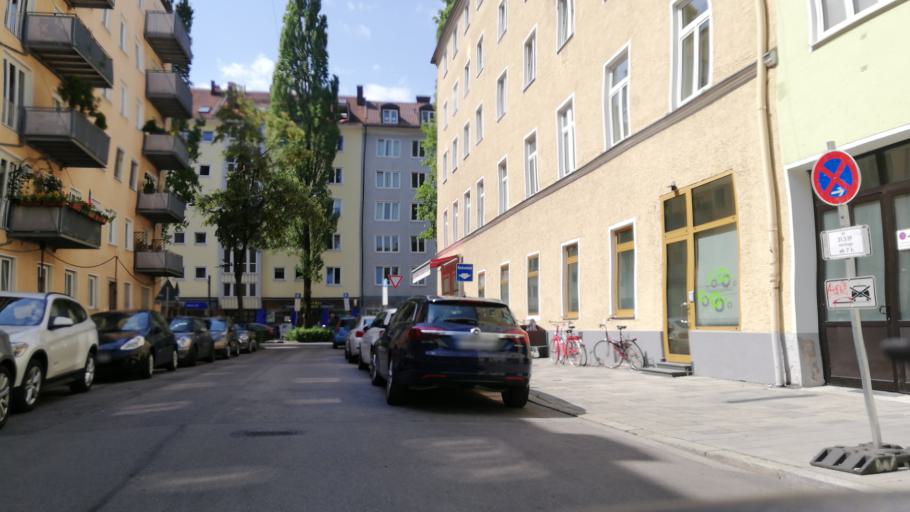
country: DE
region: Bavaria
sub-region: Upper Bavaria
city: Munich
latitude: 48.1555
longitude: 11.5658
